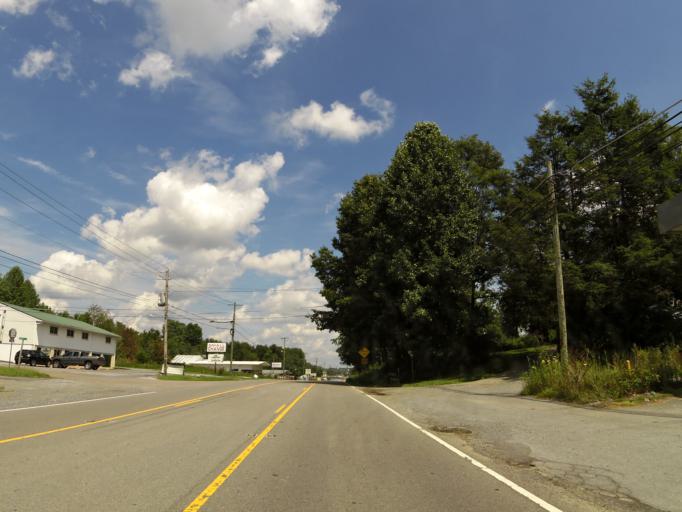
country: US
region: Virginia
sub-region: Washington County
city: Abingdon
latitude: 36.6716
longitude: -82.0551
